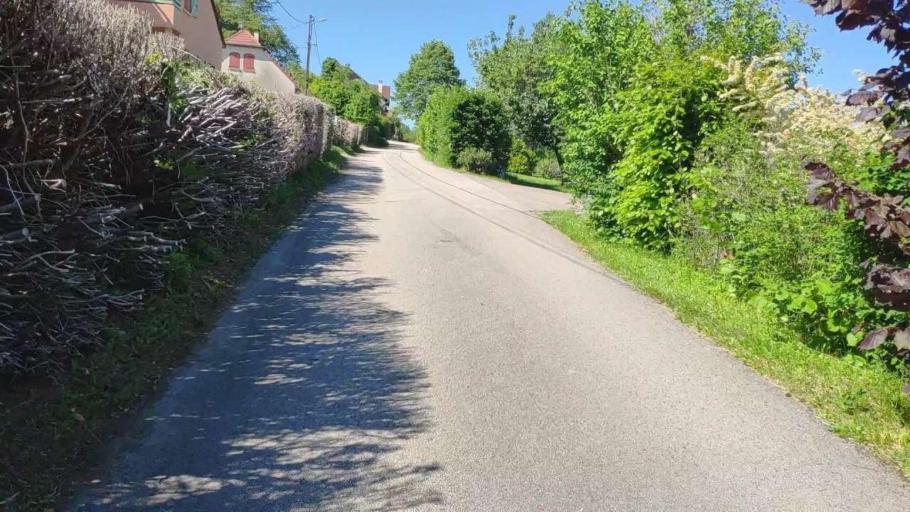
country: FR
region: Franche-Comte
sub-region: Departement du Jura
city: Perrigny
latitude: 46.7221
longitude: 5.5813
